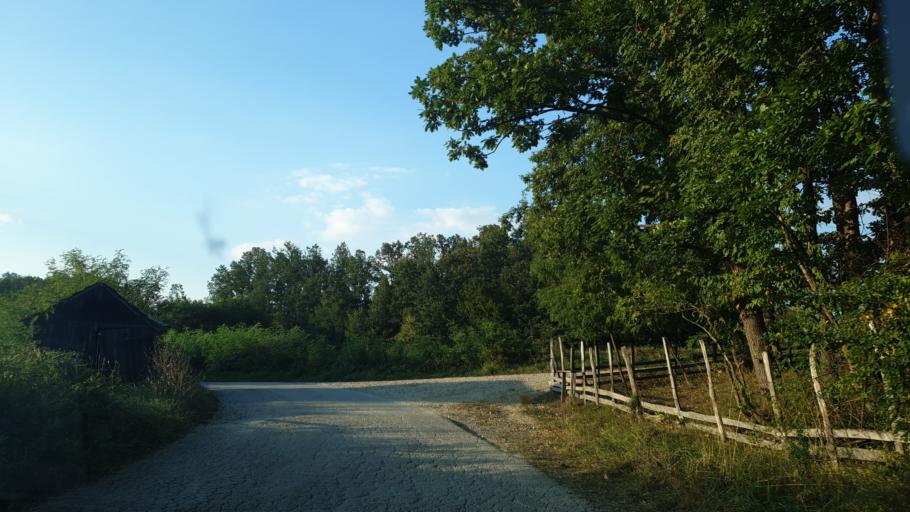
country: RS
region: Central Serbia
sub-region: Zlatiborski Okrug
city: Kosjeric
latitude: 43.9849
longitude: 20.0138
